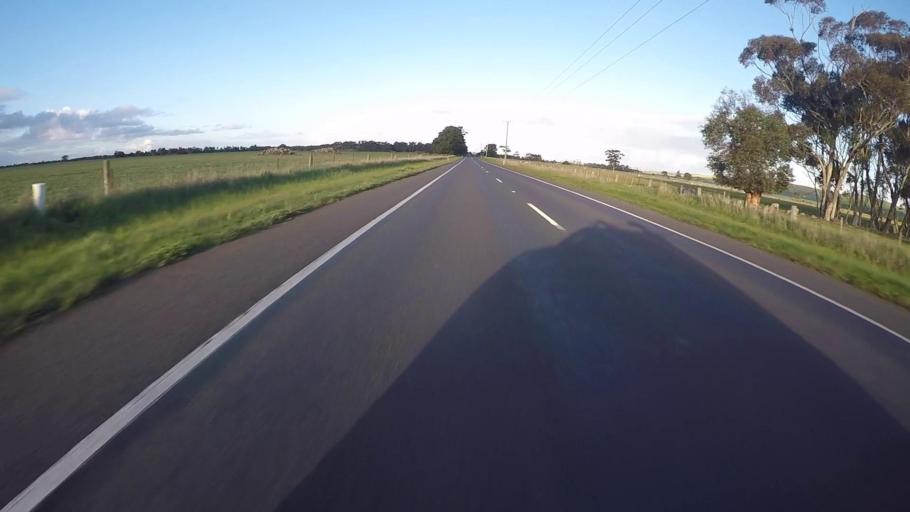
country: AU
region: Victoria
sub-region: Greater Geelong
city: Wandana Heights
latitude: -38.1221
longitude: 144.2123
